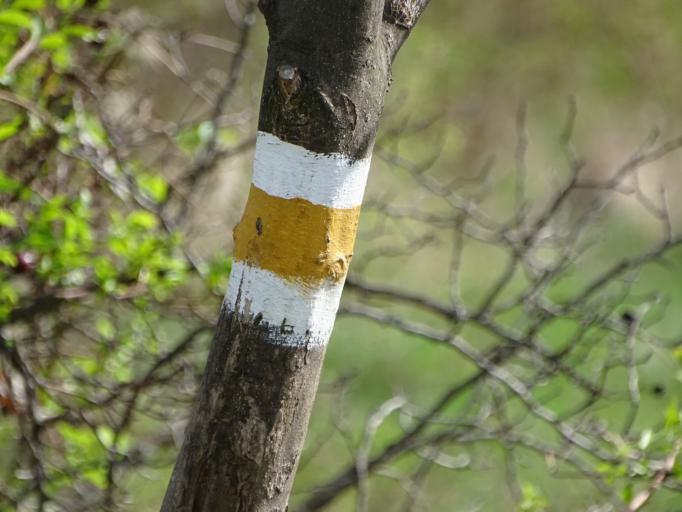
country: HU
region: Pest
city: Nagykovacsi
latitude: 47.6767
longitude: 19.0396
